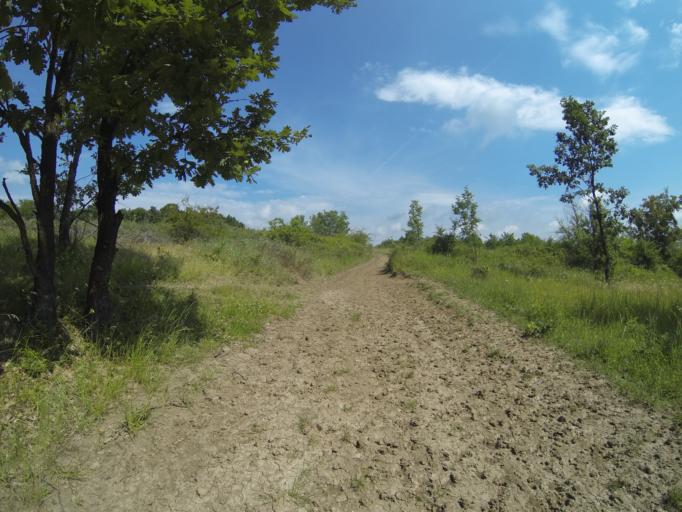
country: RO
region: Gorj
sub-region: Comuna Crusetu
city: Crusetu
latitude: 44.6247
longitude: 23.6183
